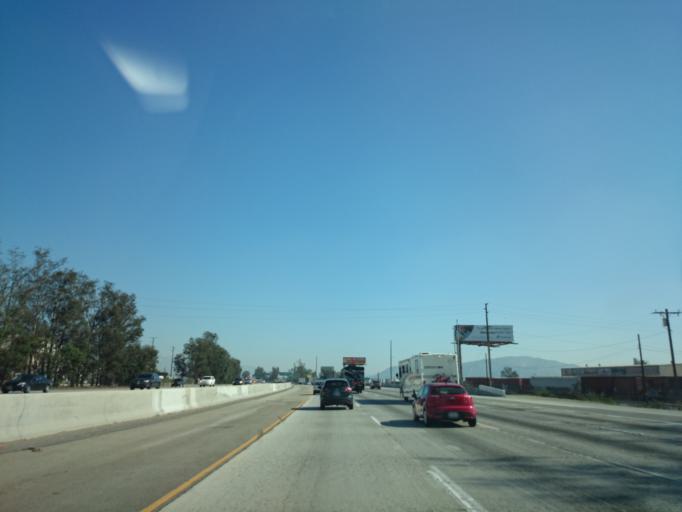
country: US
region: California
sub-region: Riverside County
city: Glen Avon
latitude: 34.0660
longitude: -117.5082
